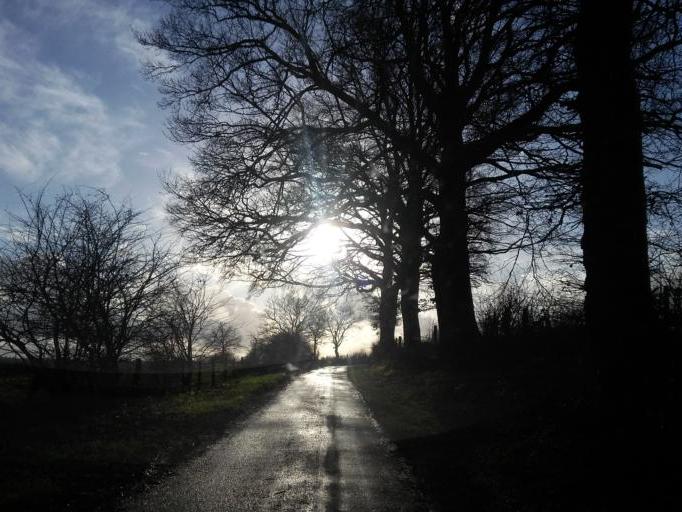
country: BE
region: Wallonia
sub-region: Province du Luxembourg
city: Neufchateau
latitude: 49.8122
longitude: 5.4423
